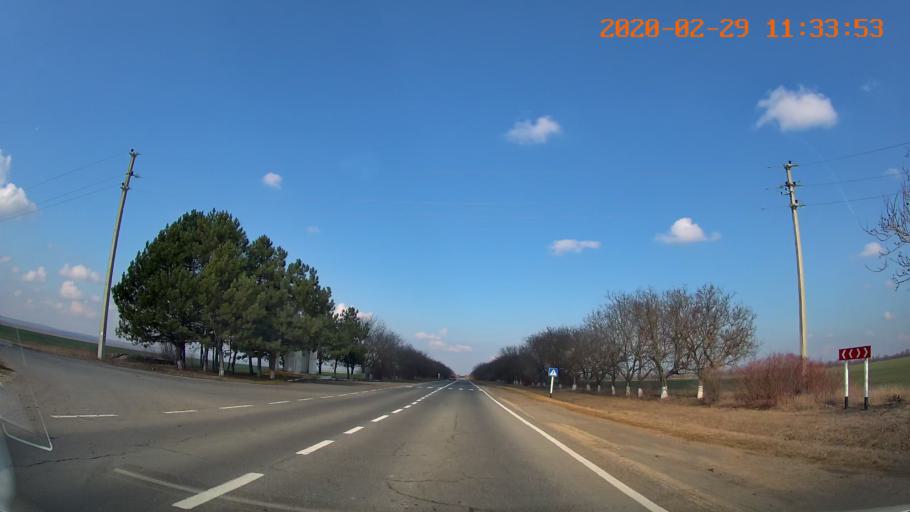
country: MD
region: Rezina
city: Saharna
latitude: 47.5577
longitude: 29.0798
